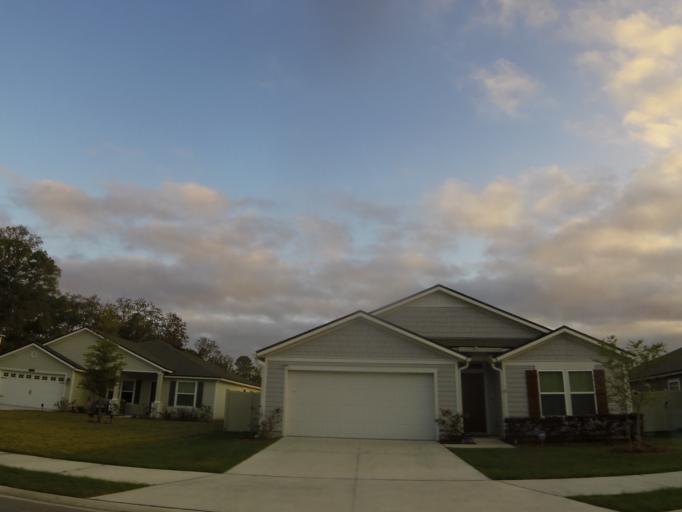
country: US
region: Florida
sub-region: Duval County
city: Jacksonville
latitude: 30.4723
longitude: -81.6224
